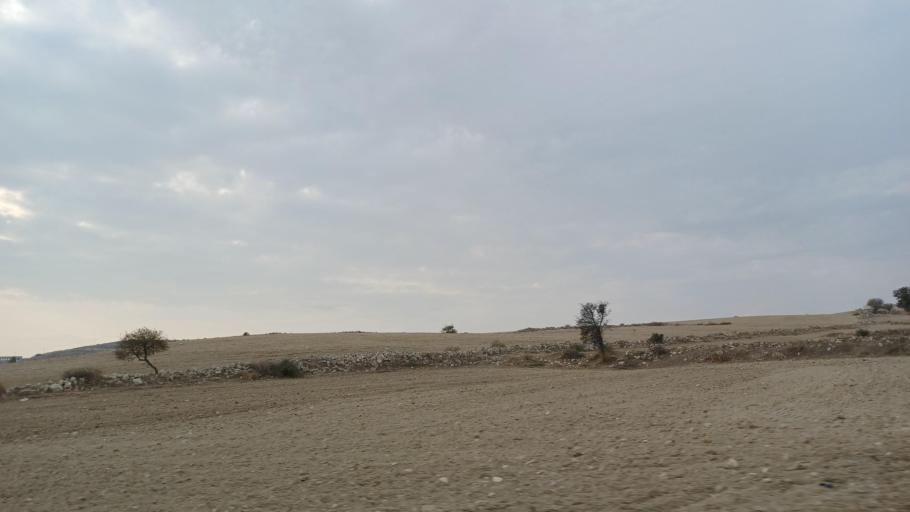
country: CY
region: Larnaka
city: Athienou
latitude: 35.0362
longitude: 33.5701
